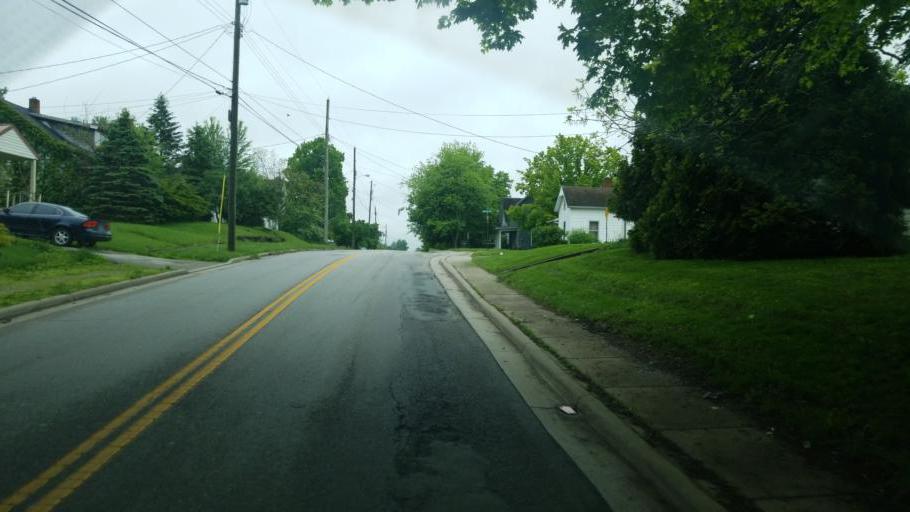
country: US
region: Ohio
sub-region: Highland County
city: Hillsboro
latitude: 39.2106
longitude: -83.6120
